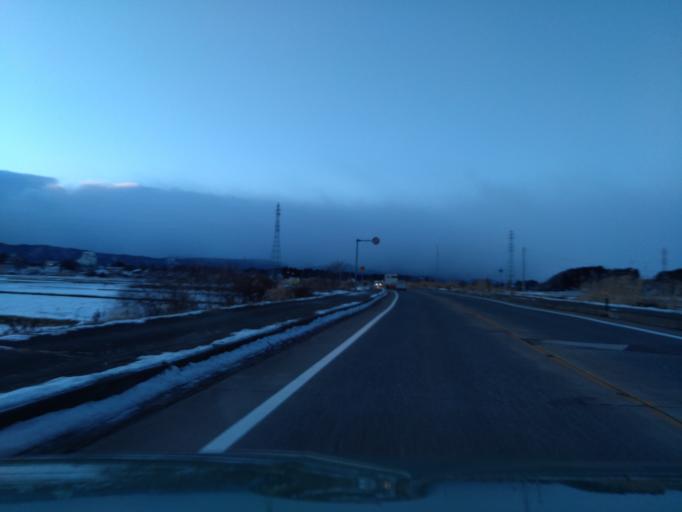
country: JP
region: Iwate
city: Shizukuishi
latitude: 39.7004
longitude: 140.9757
